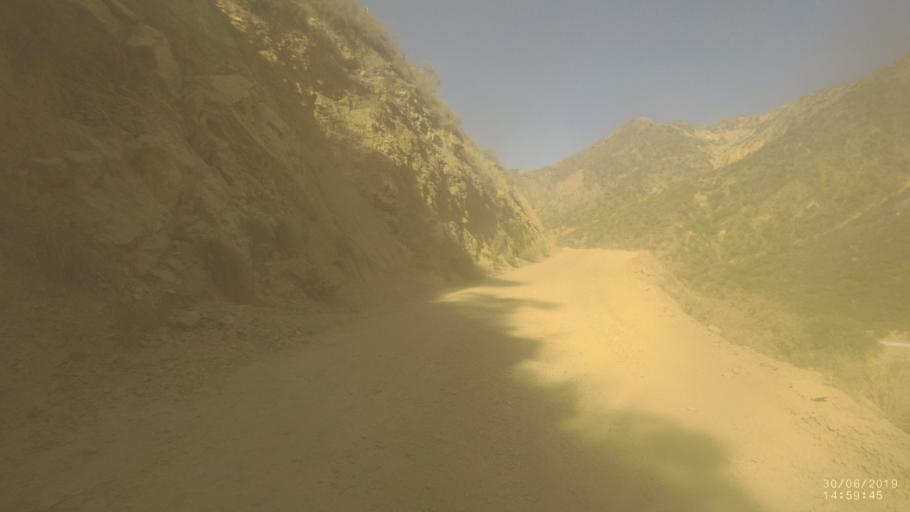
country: BO
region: Cochabamba
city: Irpa Irpa
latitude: -17.7365
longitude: -66.3437
